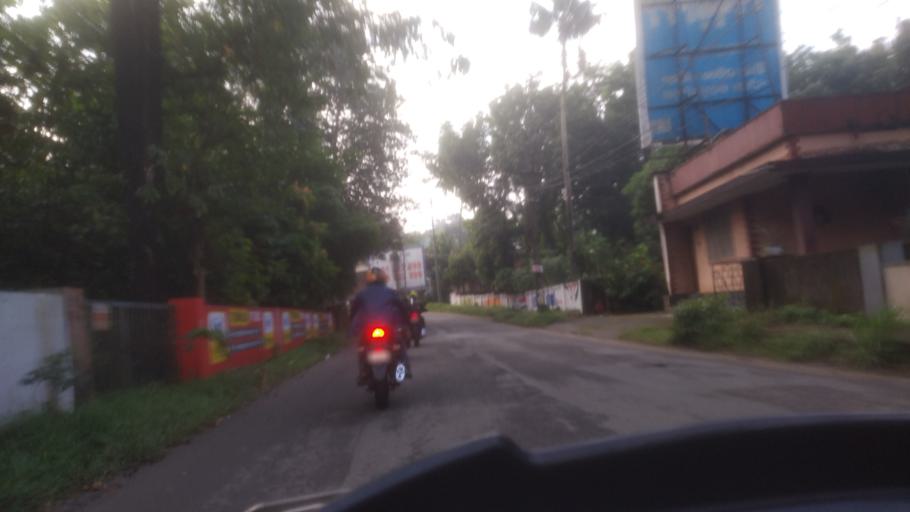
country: IN
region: Kerala
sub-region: Ernakulam
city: Perumpavur
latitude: 10.1063
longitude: 76.5361
